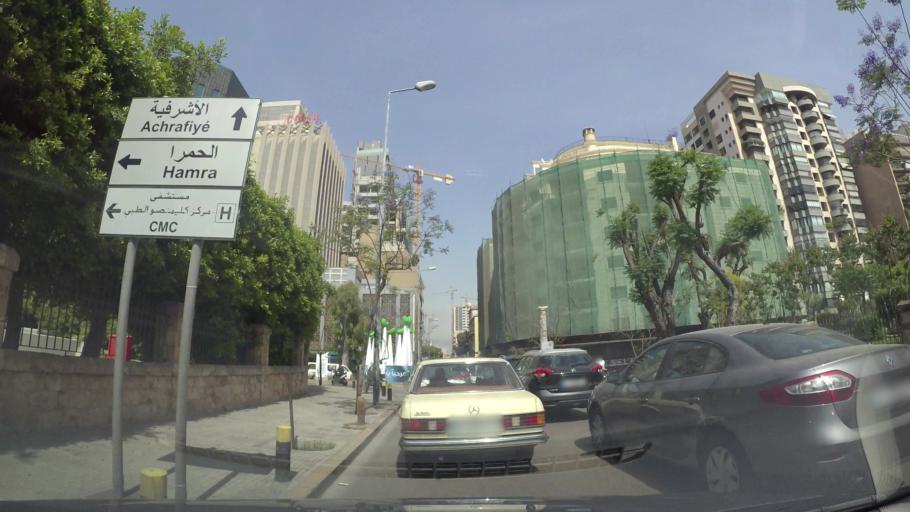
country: LB
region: Beyrouth
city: Beirut
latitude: 33.8945
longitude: 35.4907
